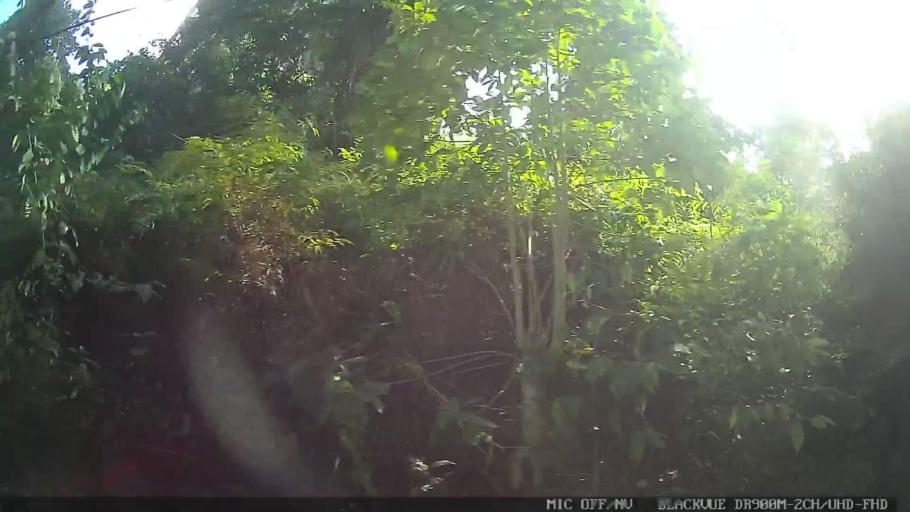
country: BR
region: Sao Paulo
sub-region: Guaruja
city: Guaruja
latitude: -23.9831
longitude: -46.1900
